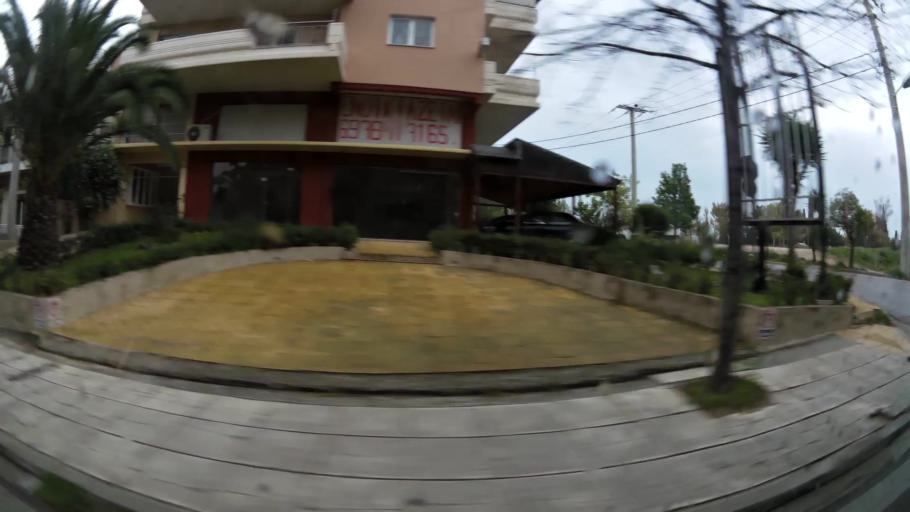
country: GR
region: Attica
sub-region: Nomarchia Athinas
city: Agioi Anargyroi
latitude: 38.0386
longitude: 23.7249
